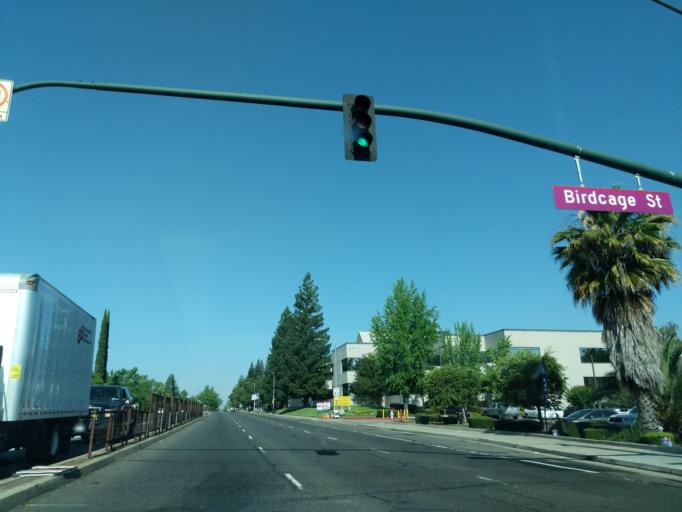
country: US
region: California
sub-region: Sacramento County
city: Citrus Heights
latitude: 38.6784
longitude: -121.2760
